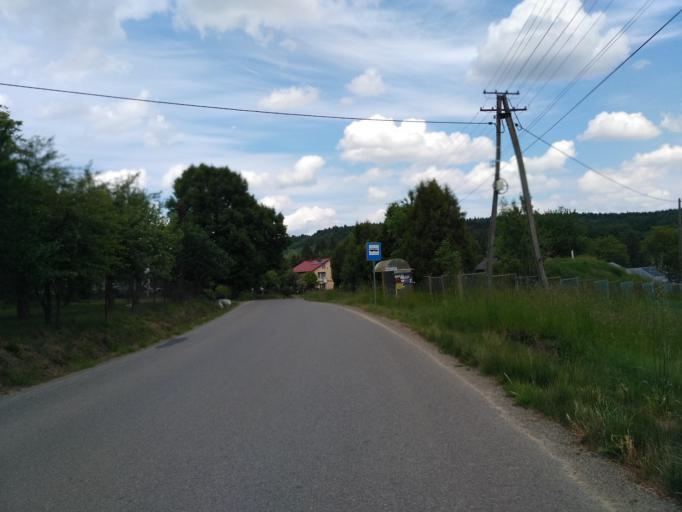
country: PL
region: Subcarpathian Voivodeship
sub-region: Powiat krosnienski
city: Chorkowka
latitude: 49.6155
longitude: 21.6479
